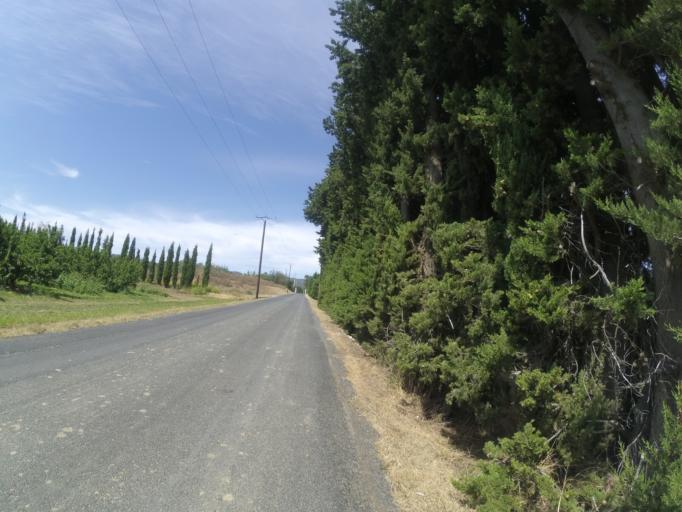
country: FR
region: Languedoc-Roussillon
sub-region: Departement des Pyrenees-Orientales
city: Millas
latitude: 42.6793
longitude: 2.6690
